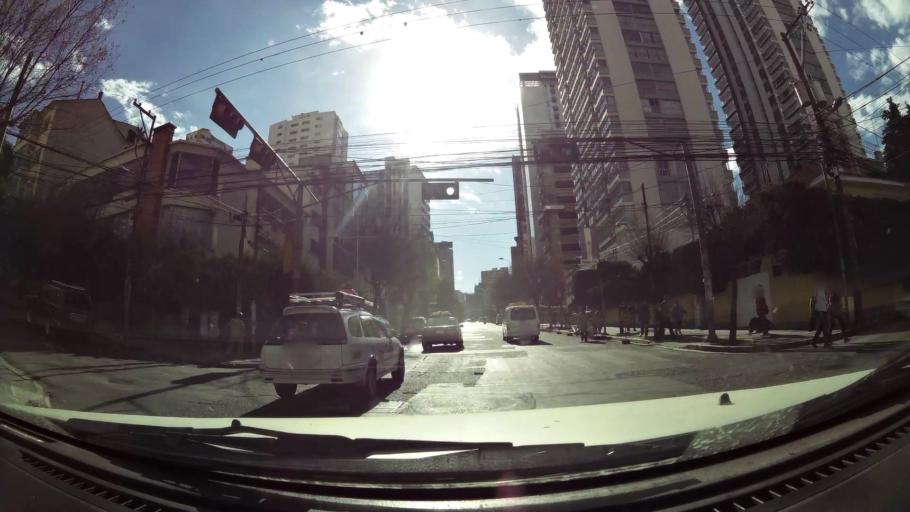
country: BO
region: La Paz
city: La Paz
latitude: -16.5085
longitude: -68.1252
